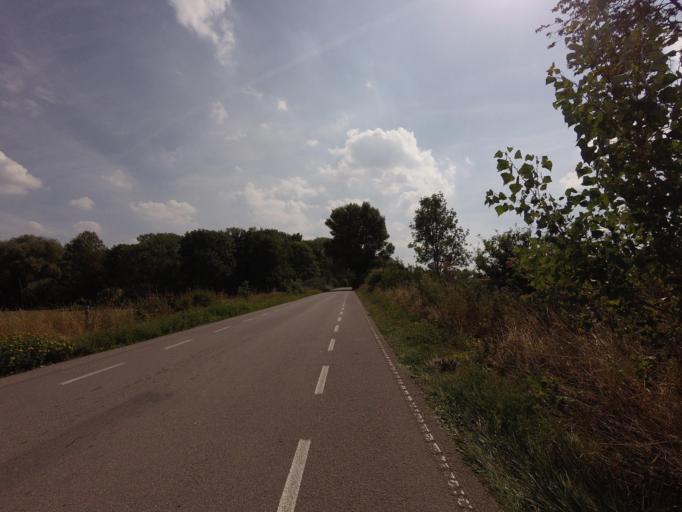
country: NL
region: Gelderland
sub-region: Gemeente Rheden
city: De Steeg
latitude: 52.0104
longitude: 6.0782
